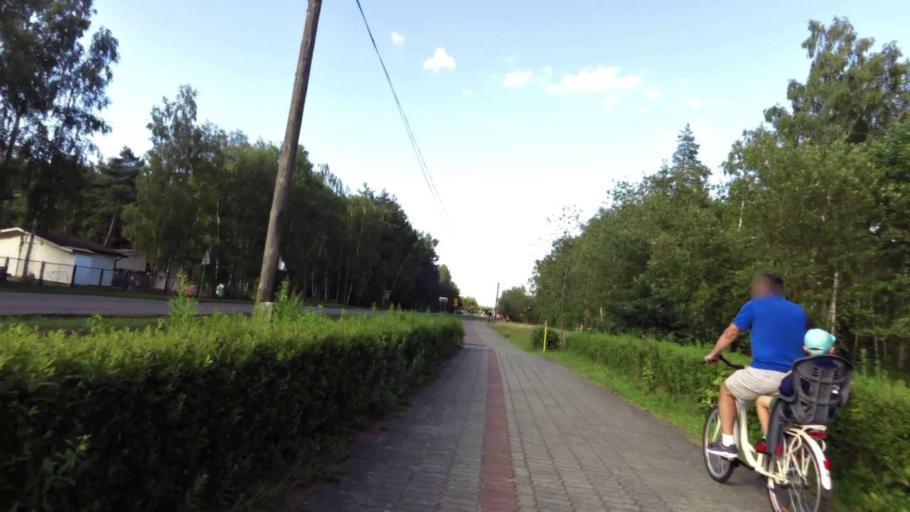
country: PL
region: West Pomeranian Voivodeship
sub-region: Powiat slawienski
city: Darlowo
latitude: 54.3861
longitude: 16.3275
